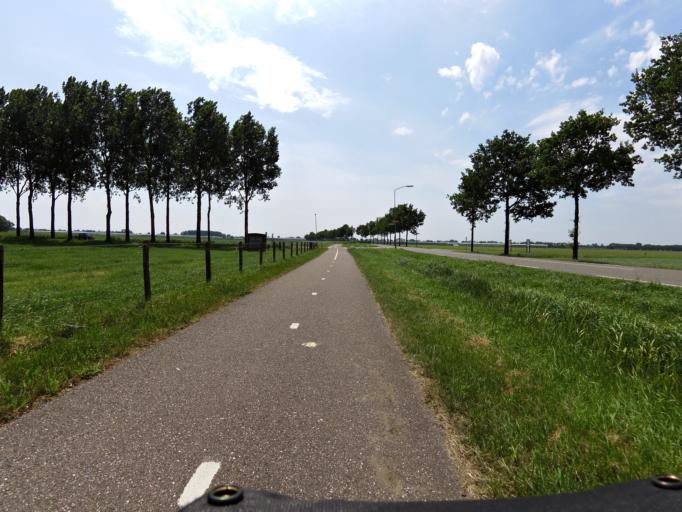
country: NL
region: North Brabant
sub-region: Gemeente Aalburg
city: Aalburg
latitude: 51.8008
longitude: 5.0840
